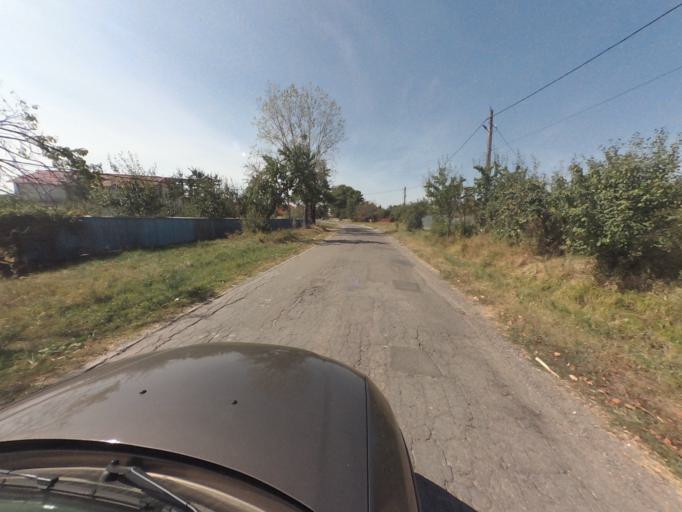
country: RO
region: Vaslui
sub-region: Comuna Deleni
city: Deleni
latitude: 46.5434
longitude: 27.7515
